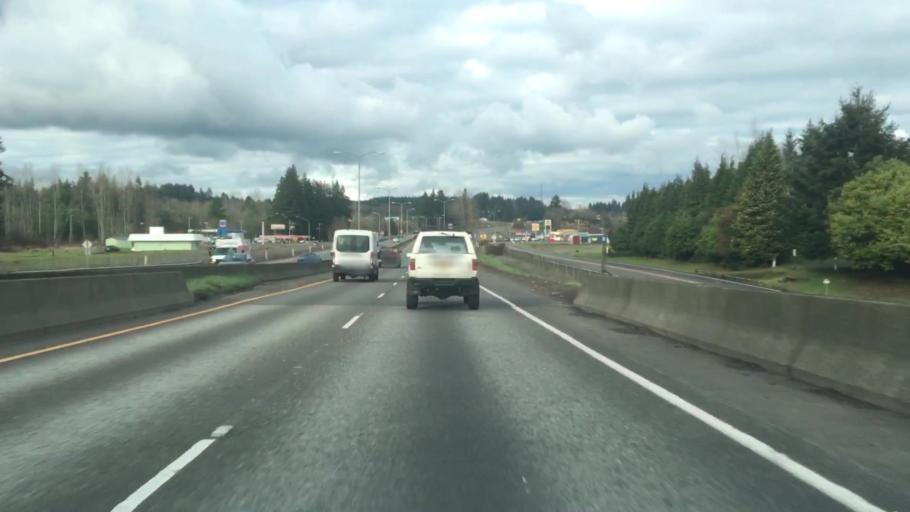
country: US
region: Washington
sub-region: Lewis County
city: Winlock
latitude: 46.4149
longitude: -122.8902
